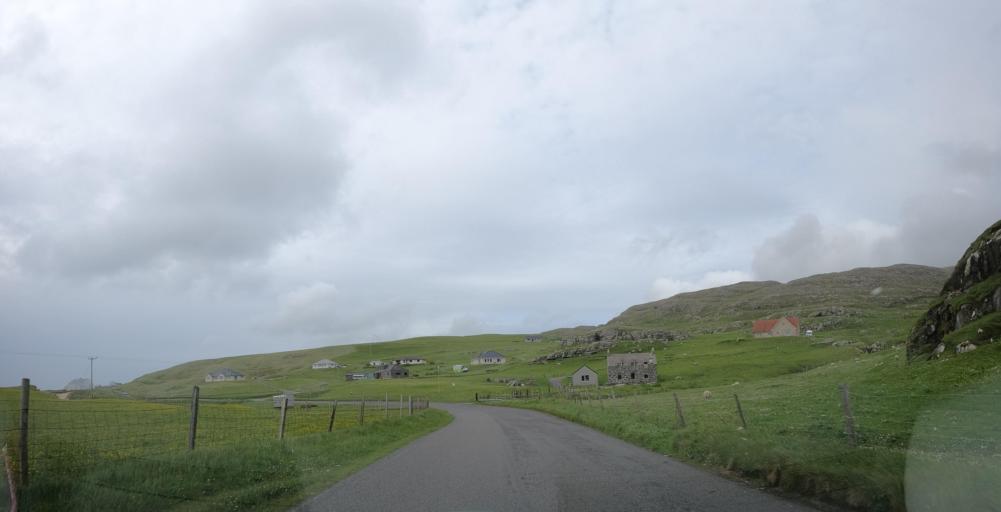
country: GB
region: Scotland
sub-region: Eilean Siar
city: Barra
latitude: 56.9720
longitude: -7.5153
